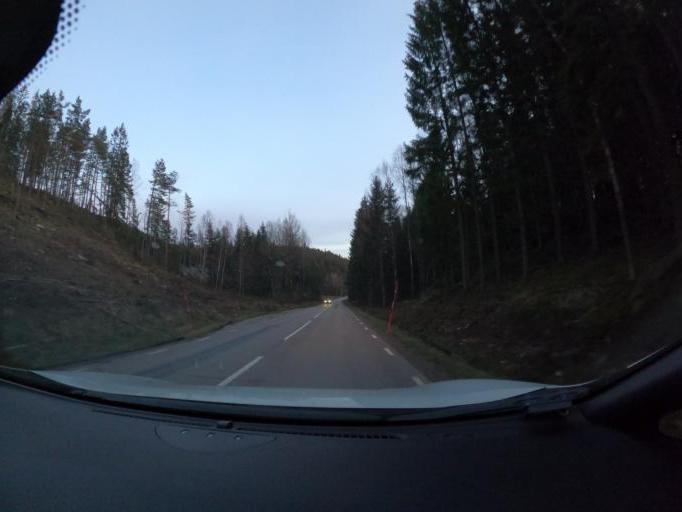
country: SE
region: Vaestra Goetaland
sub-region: Harryda Kommun
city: Landvetter
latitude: 57.6264
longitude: 12.1814
